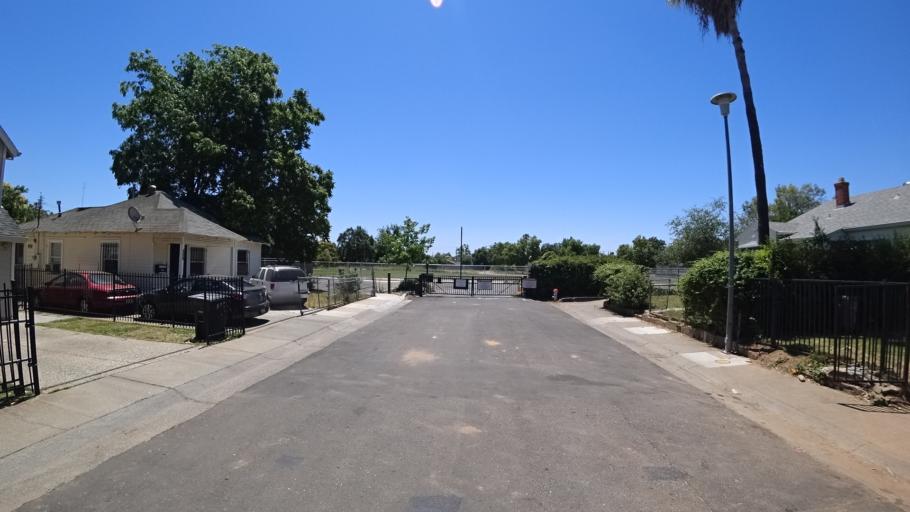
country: US
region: California
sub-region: Sacramento County
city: Parkway
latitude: 38.5433
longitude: -121.4620
